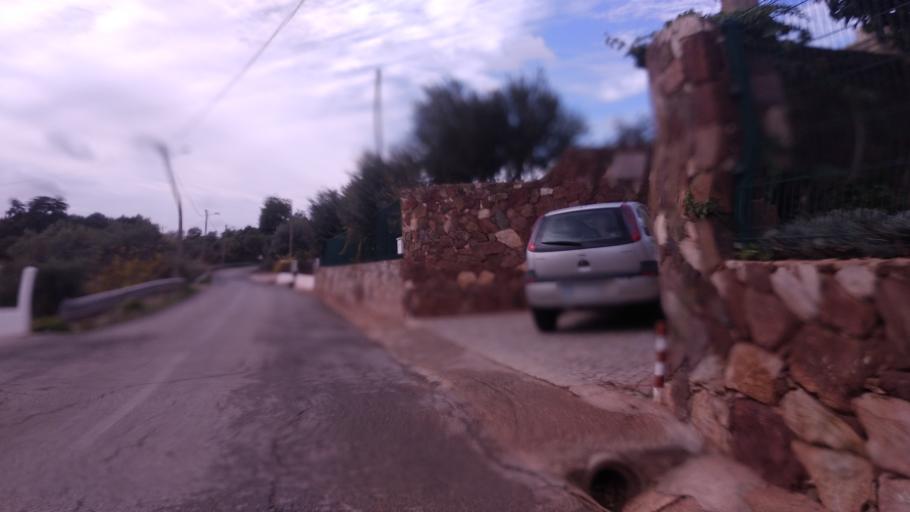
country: PT
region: Faro
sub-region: Sao Bras de Alportel
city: Sao Bras de Alportel
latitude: 37.1753
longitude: -7.9026
